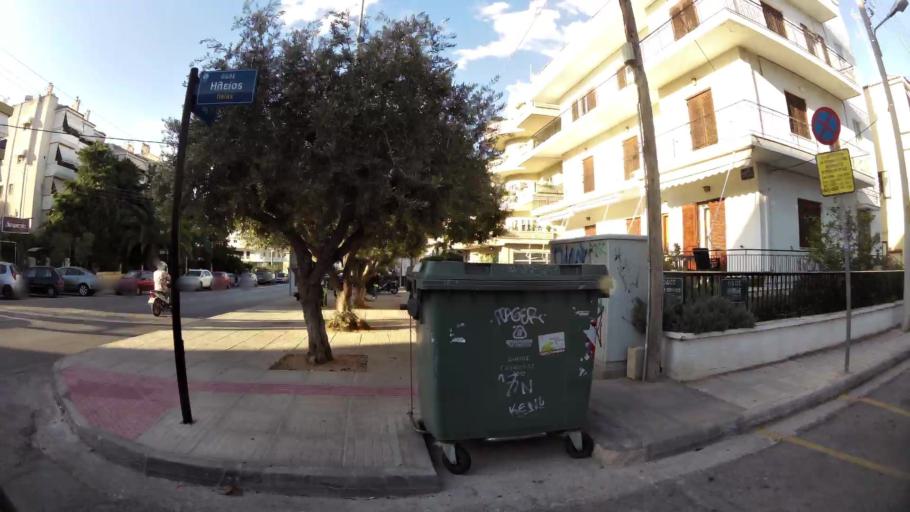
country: GR
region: Attica
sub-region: Nomarchia Athinas
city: Elliniko
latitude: 37.8849
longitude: 23.7482
